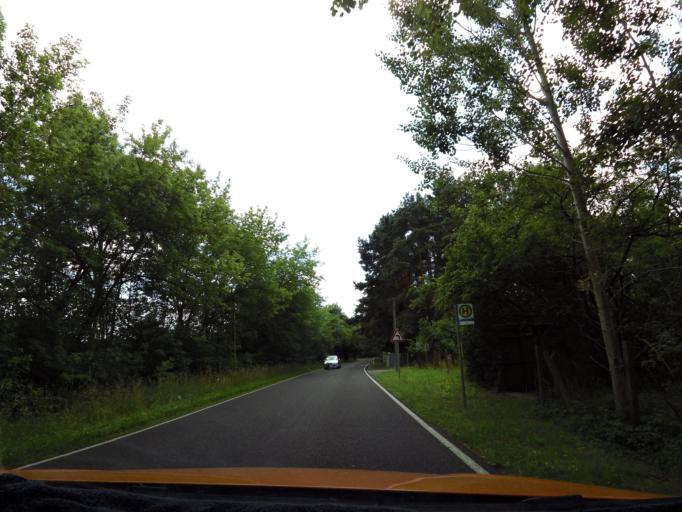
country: DE
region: Brandenburg
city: Munchehofe
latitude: 52.2521
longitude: 13.7914
